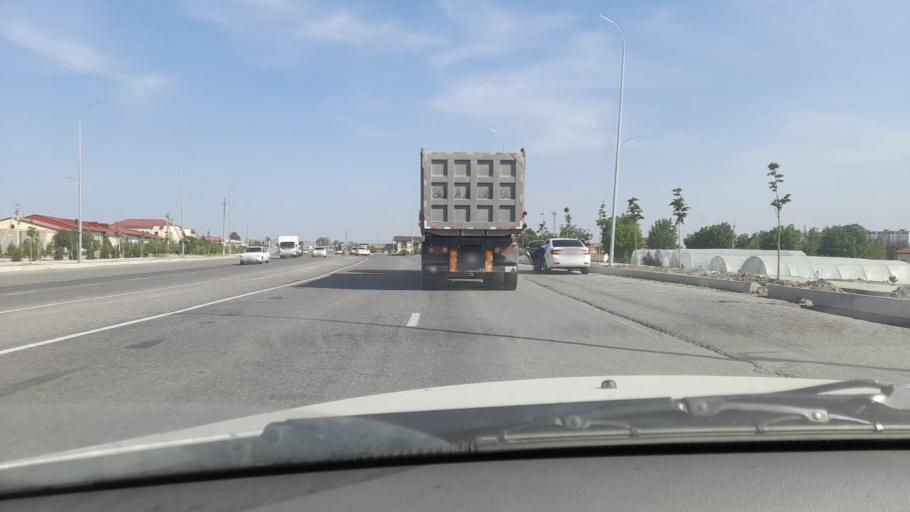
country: UZ
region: Samarqand
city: Daxbet
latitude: 39.7316
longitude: 66.9365
